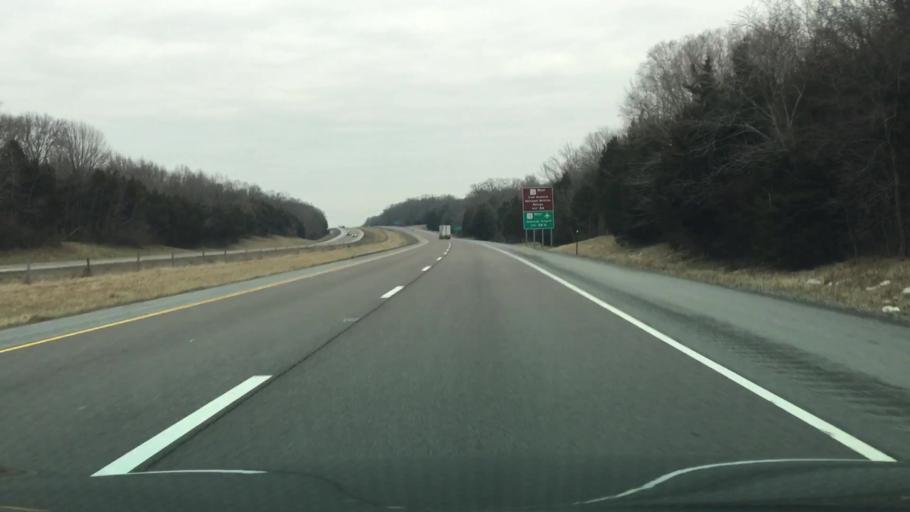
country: US
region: Illinois
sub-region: Williamson County
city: Marion
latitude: 37.6767
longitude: -88.9665
